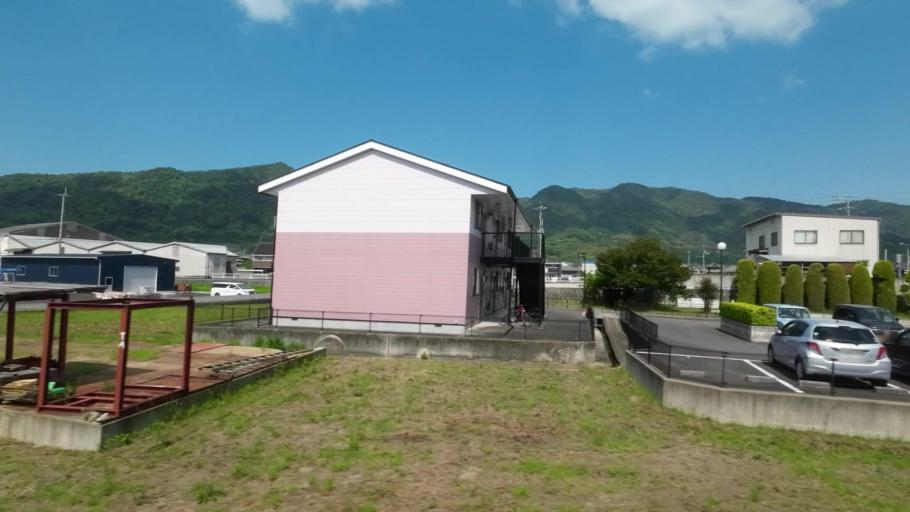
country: JP
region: Kagawa
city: Kan'onjicho
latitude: 34.1626
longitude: 133.6895
